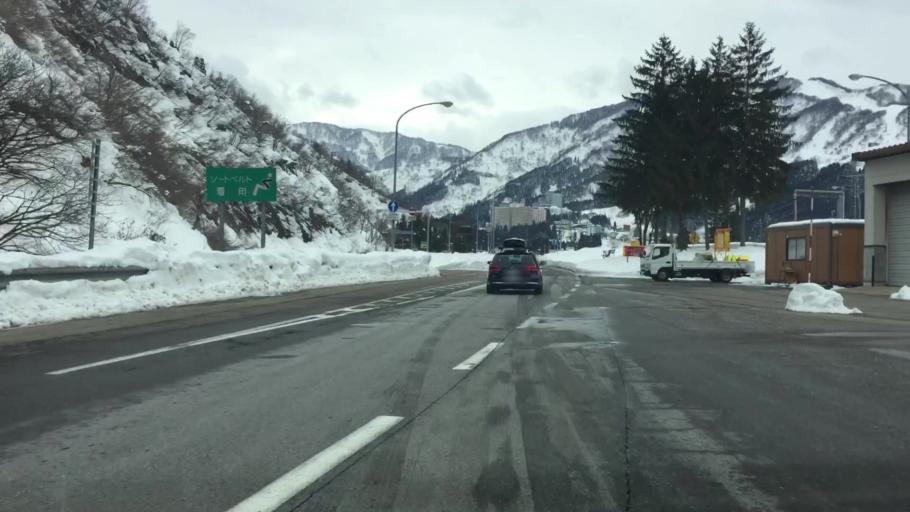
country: JP
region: Niigata
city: Shiozawa
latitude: 36.9792
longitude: 138.8117
